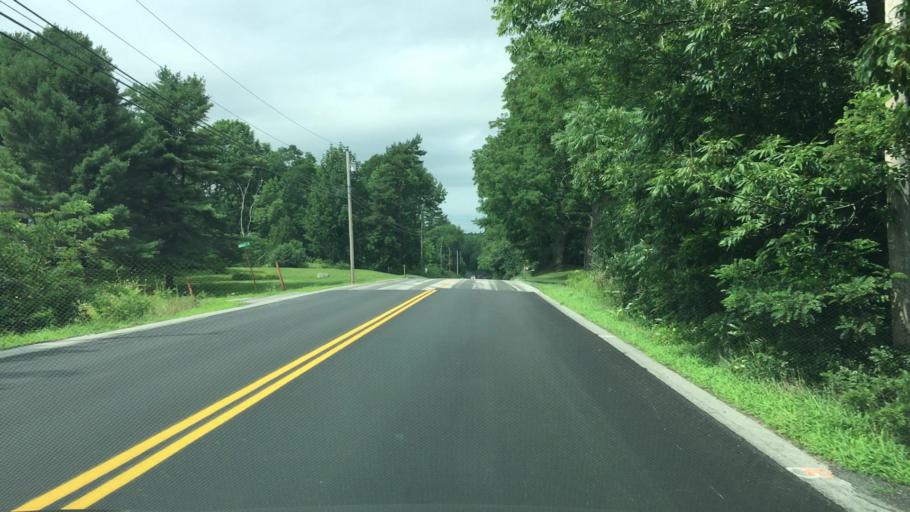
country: US
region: Maine
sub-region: Waldo County
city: Winterport
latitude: 44.6085
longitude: -68.8209
